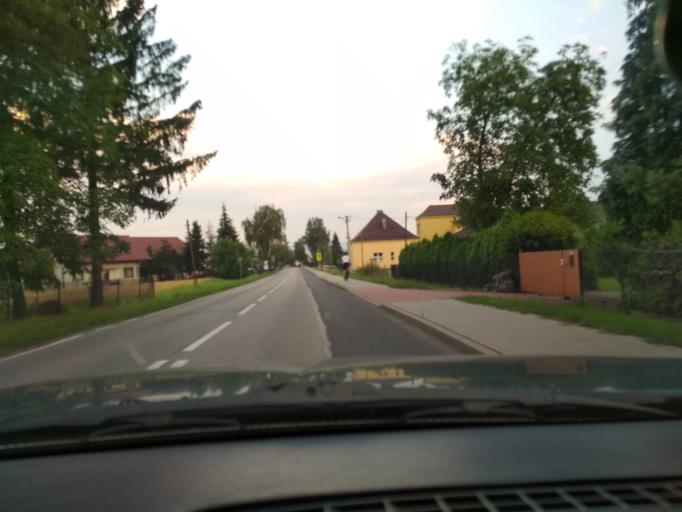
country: PL
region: Silesian Voivodeship
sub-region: Powiat cieszynski
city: Zablocie
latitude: 49.9049
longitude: 18.7775
